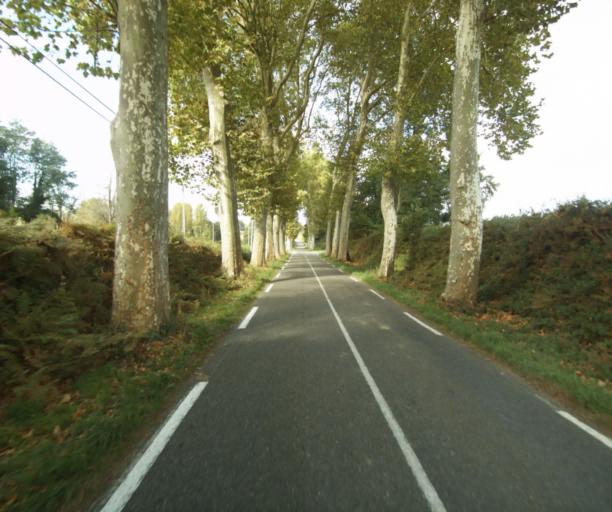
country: FR
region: Midi-Pyrenees
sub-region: Departement du Gers
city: Cazaubon
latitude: 43.8660
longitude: -0.0721
